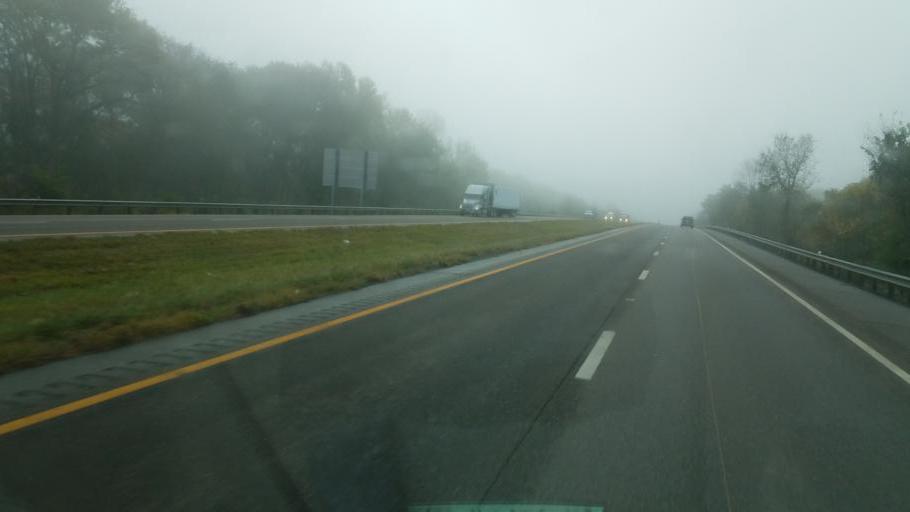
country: US
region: Ohio
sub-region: Tuscarawas County
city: New Philadelphia
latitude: 40.4657
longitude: -81.4287
